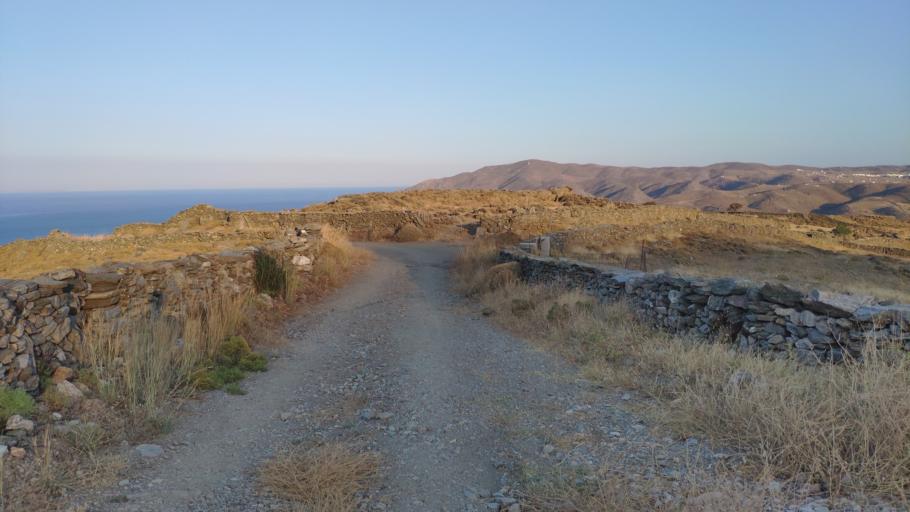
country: GR
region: South Aegean
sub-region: Nomos Kykladon
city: Kythnos
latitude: 37.4571
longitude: 24.4175
